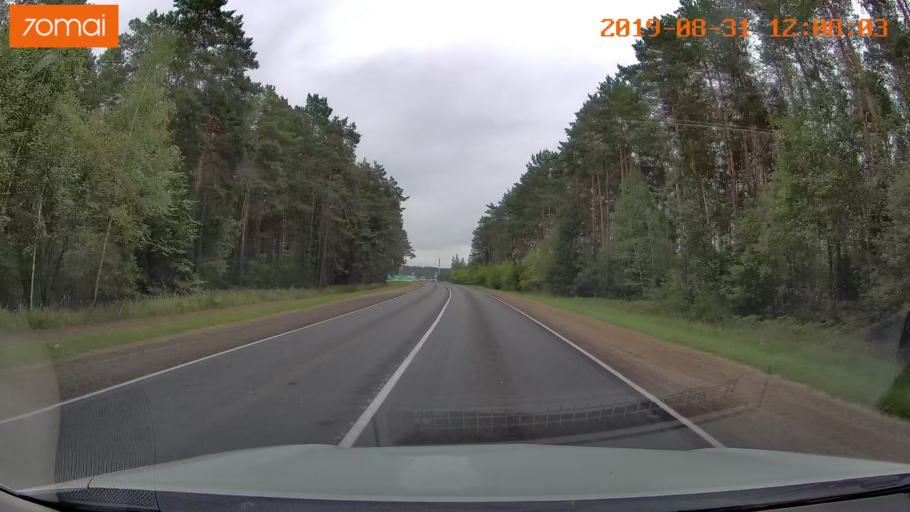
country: BY
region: Mogilev
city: Krychaw
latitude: 53.7021
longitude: 31.7793
